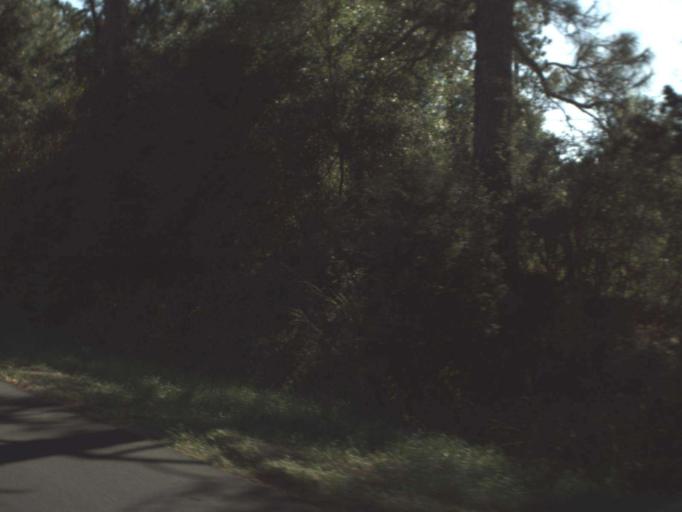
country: US
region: Florida
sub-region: Walton County
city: DeFuniak Springs
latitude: 30.7522
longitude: -86.1490
